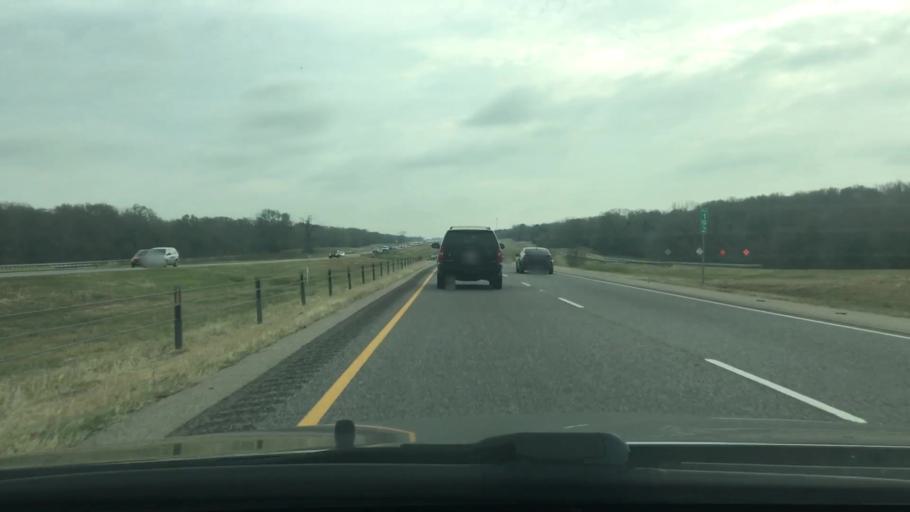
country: US
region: Texas
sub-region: Freestone County
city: Fairfield
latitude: 31.6290
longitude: -96.1579
